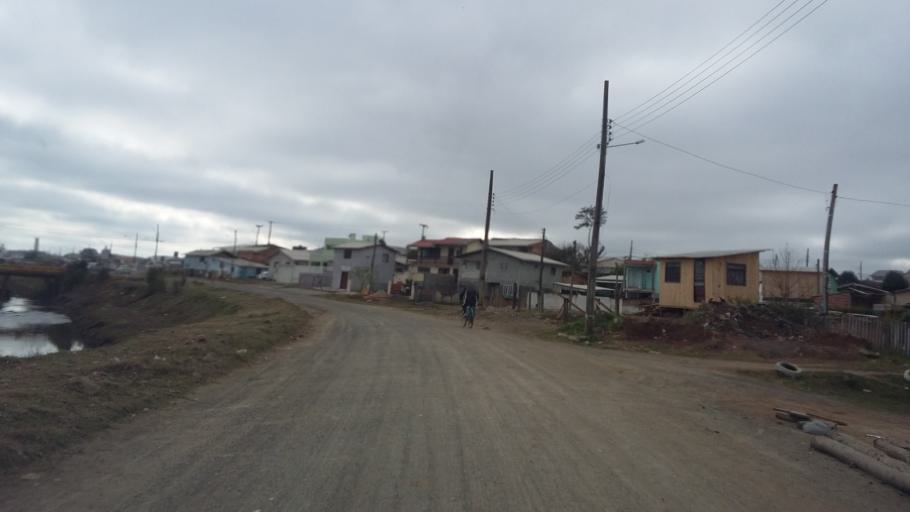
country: BR
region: Santa Catarina
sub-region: Lages
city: Lages
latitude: -27.8352
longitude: -50.3210
